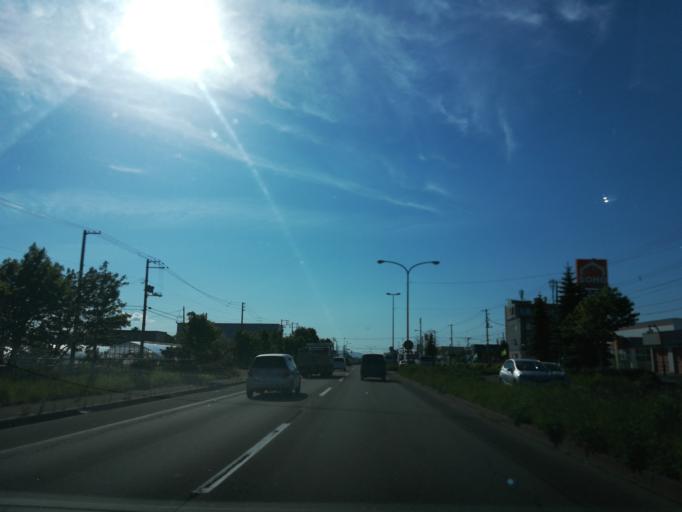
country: JP
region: Hokkaido
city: Kitahiroshima
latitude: 43.0134
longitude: 141.5040
